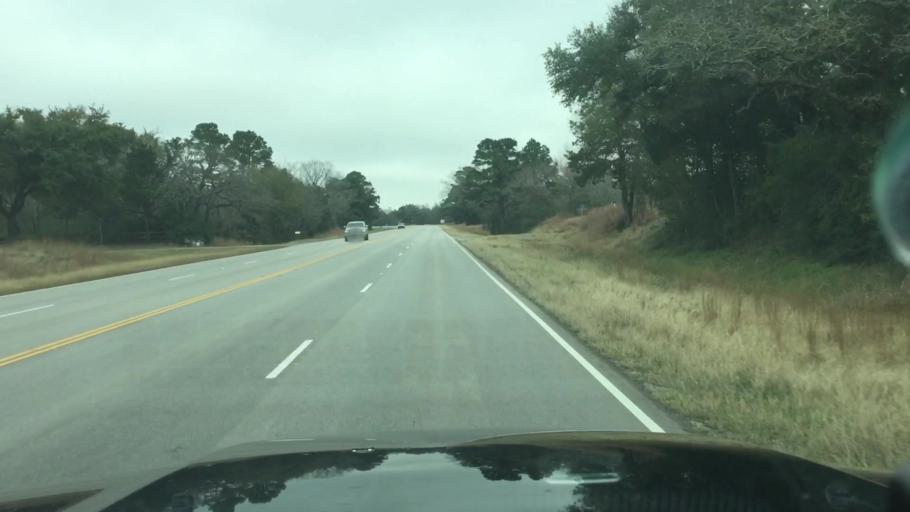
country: US
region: Texas
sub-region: Lee County
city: Giddings
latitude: 30.0893
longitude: -96.9143
